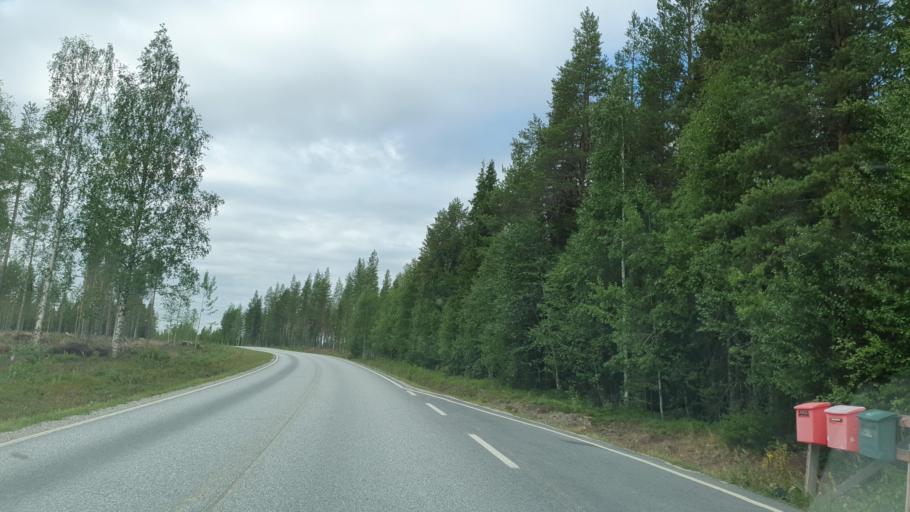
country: FI
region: Lapland
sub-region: Tunturi-Lappi
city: Kittilae
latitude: 67.6116
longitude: 25.2491
